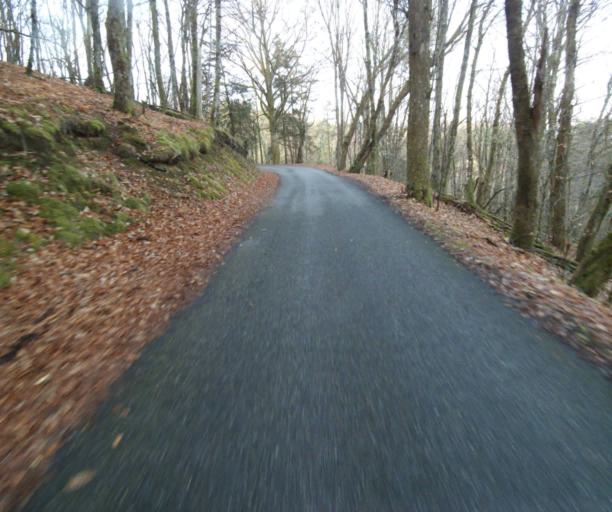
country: FR
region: Limousin
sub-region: Departement de la Correze
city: Correze
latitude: 45.2962
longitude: 1.8471
